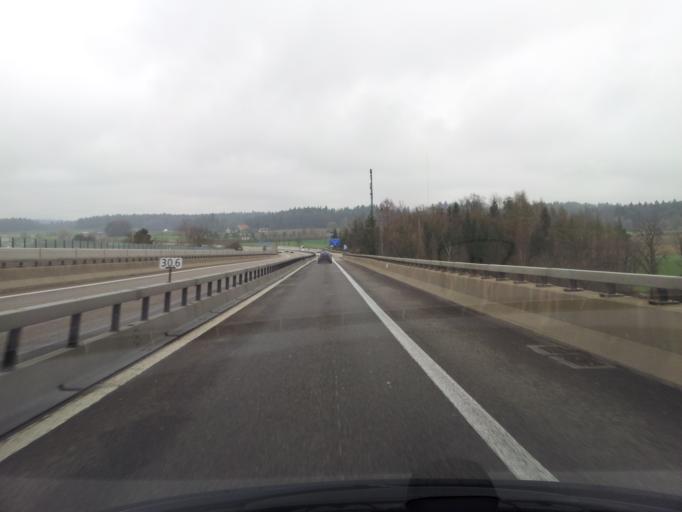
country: CH
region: Zurich
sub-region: Bezirk Andelfingen
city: Kleinandelfingen
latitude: 47.5970
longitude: 8.6905
